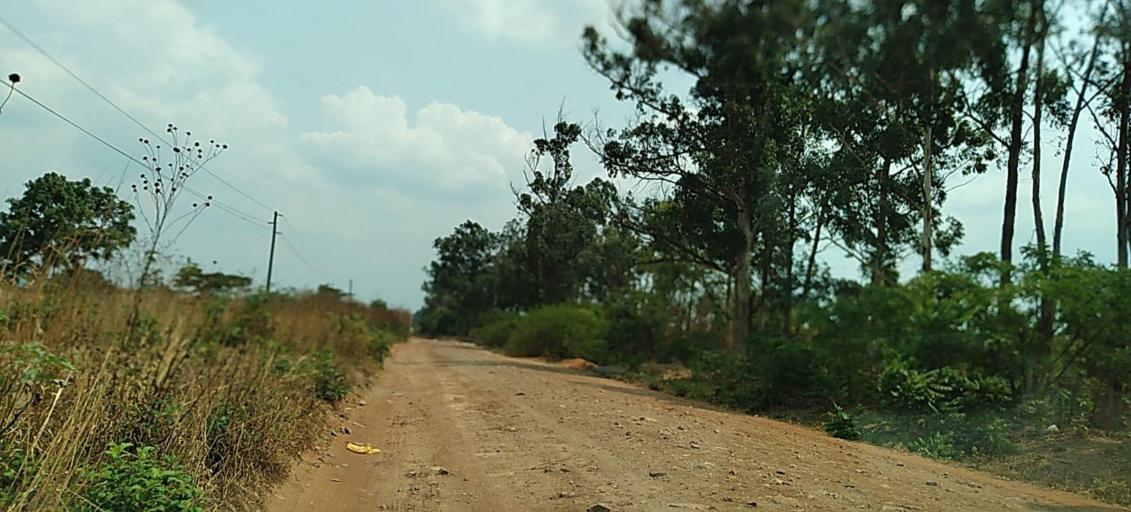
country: ZM
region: Copperbelt
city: Kalulushi
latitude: -12.8301
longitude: 28.0773
